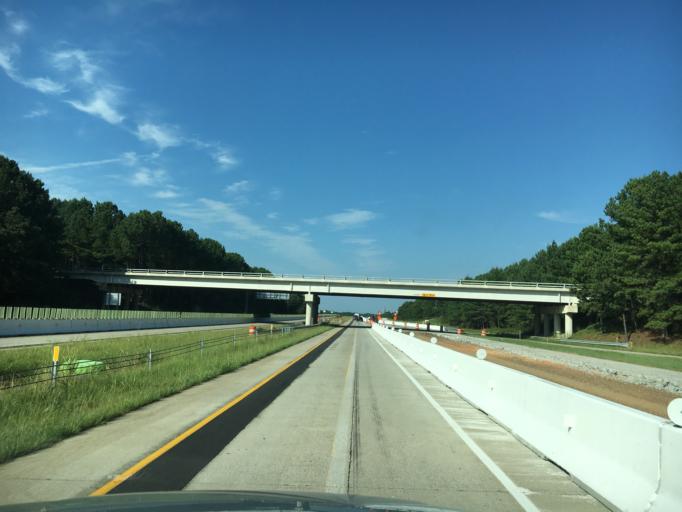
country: US
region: South Carolina
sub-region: Spartanburg County
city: Southern Shops
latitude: 34.9992
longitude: -81.9904
